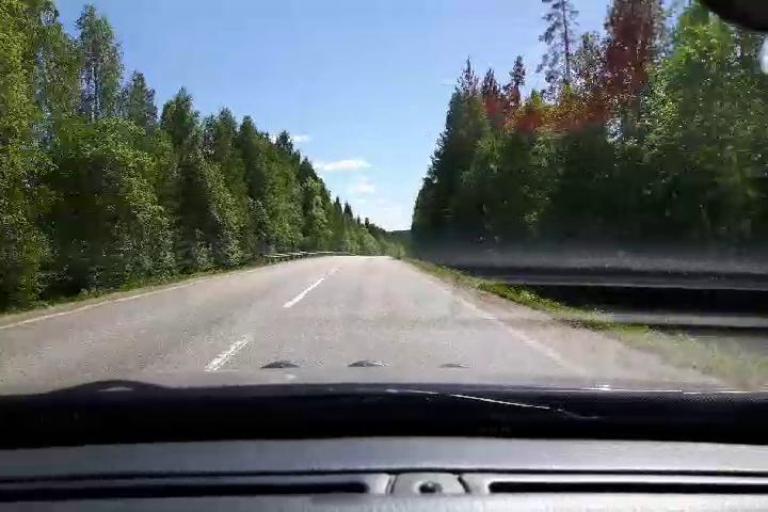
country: SE
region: Vaesternorrland
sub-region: Ange Kommun
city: Ange
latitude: 62.0793
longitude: 15.0993
